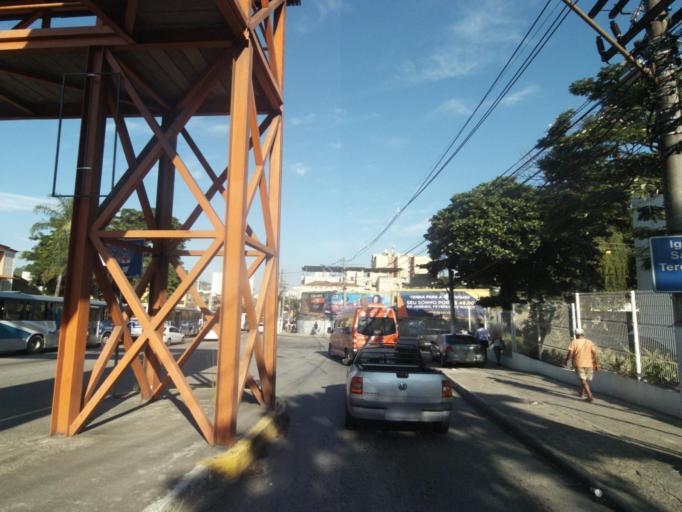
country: BR
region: Rio de Janeiro
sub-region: Niteroi
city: Niteroi
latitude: -22.8814
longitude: -43.0786
